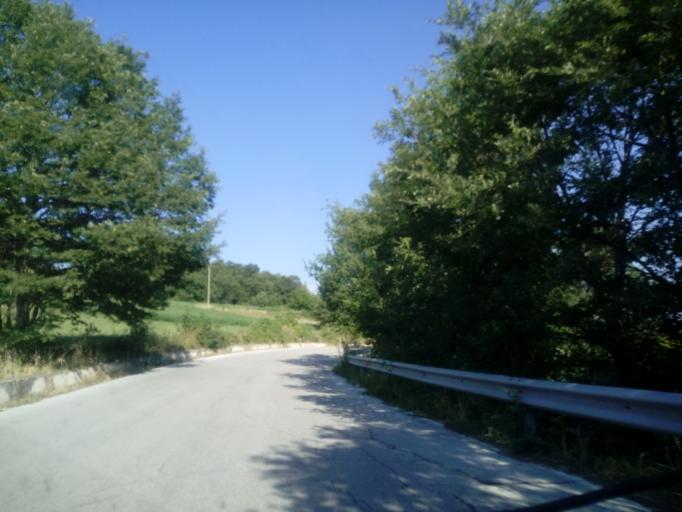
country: IT
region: Molise
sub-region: Provincia di Campobasso
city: Gildone
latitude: 41.5157
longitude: 14.7578
